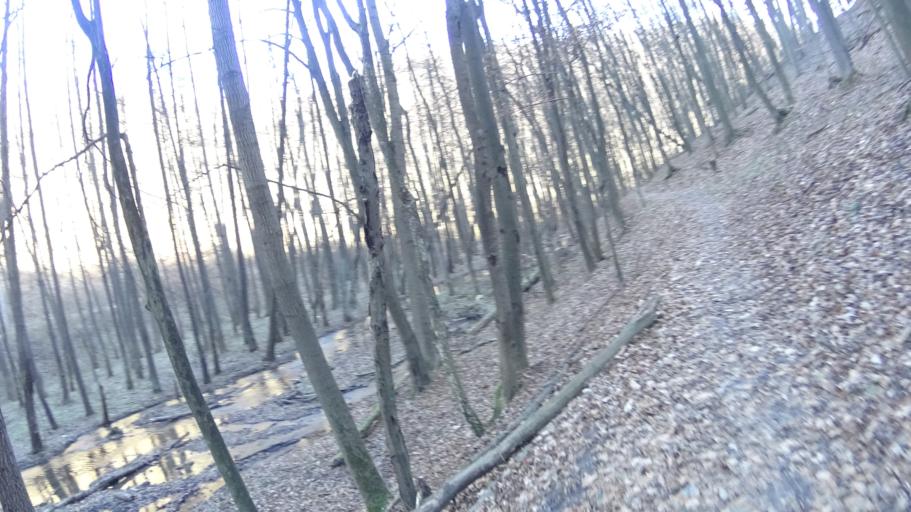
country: HU
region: Borsod-Abauj-Zemplen
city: Sajobabony
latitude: 48.1119
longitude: 20.6102
